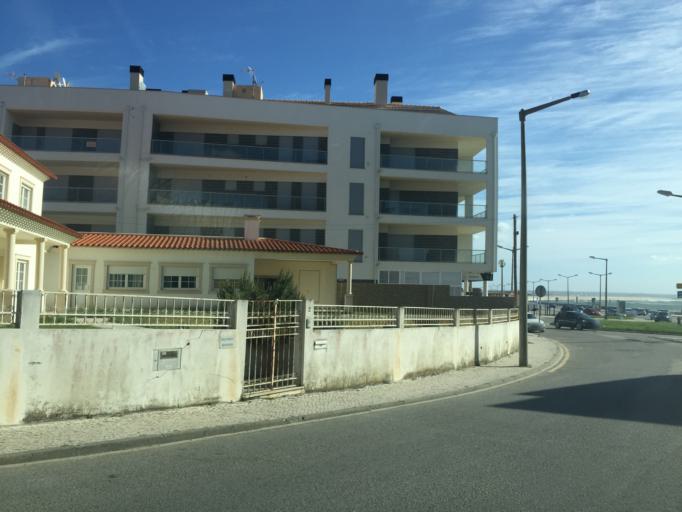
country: PT
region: Coimbra
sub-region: Figueira da Foz
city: Buarcos
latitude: 40.1672
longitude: -8.8822
